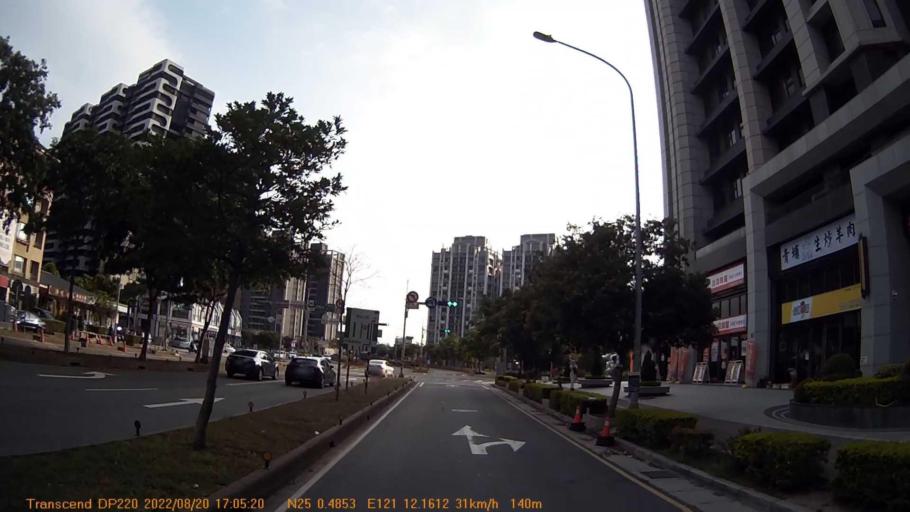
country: TW
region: Taiwan
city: Taoyuan City
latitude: 25.0080
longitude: 121.2024
